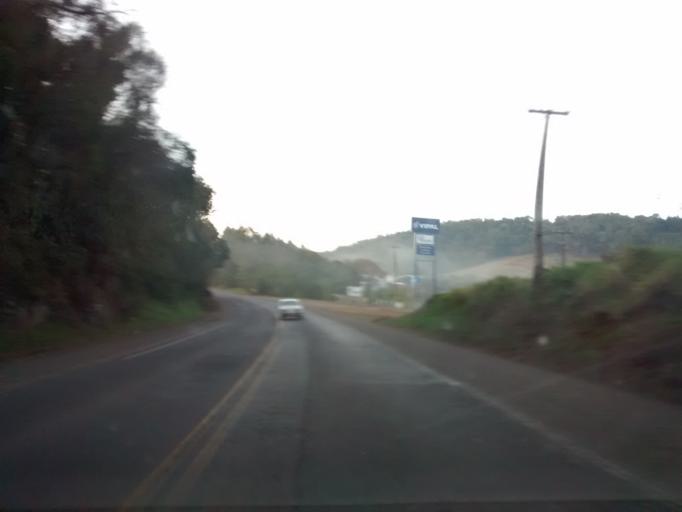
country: BR
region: Parana
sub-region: Francisco Beltrao
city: Francisco Beltrao
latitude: -26.1097
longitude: -53.0552
